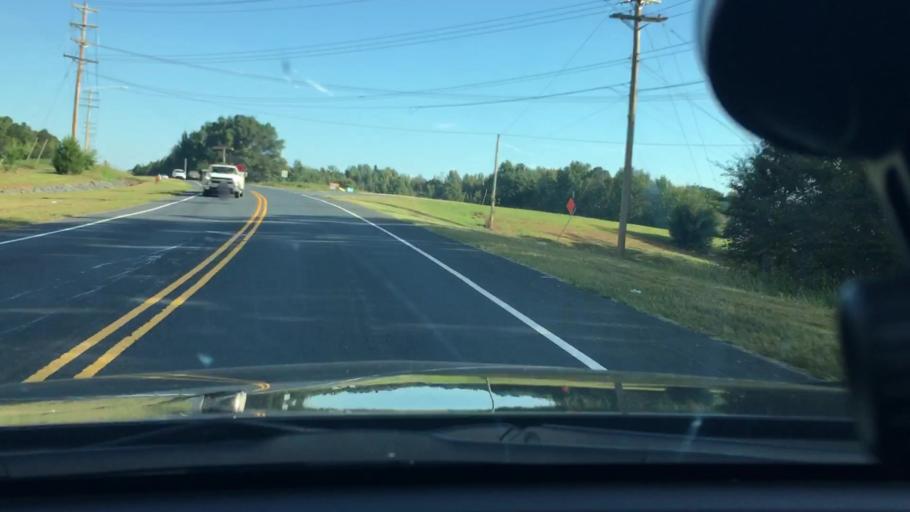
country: US
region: North Carolina
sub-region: Stanly County
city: Albemarle
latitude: 35.3673
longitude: -80.1702
